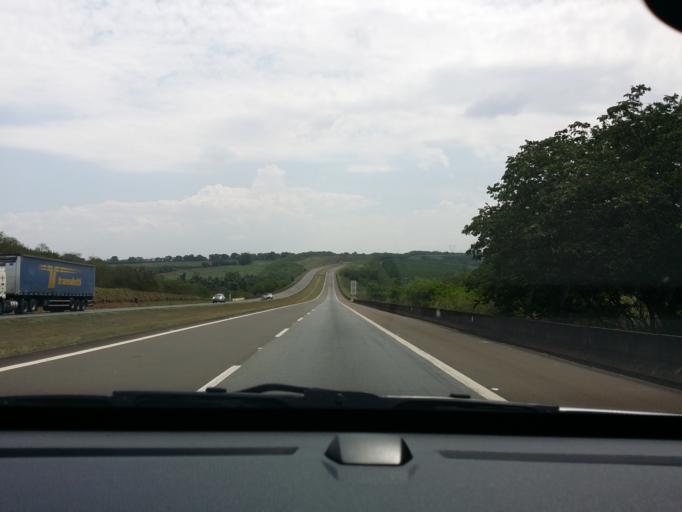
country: BR
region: Sao Paulo
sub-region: Iracemapolis
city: Iracemapolis
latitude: -22.6282
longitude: -47.4572
